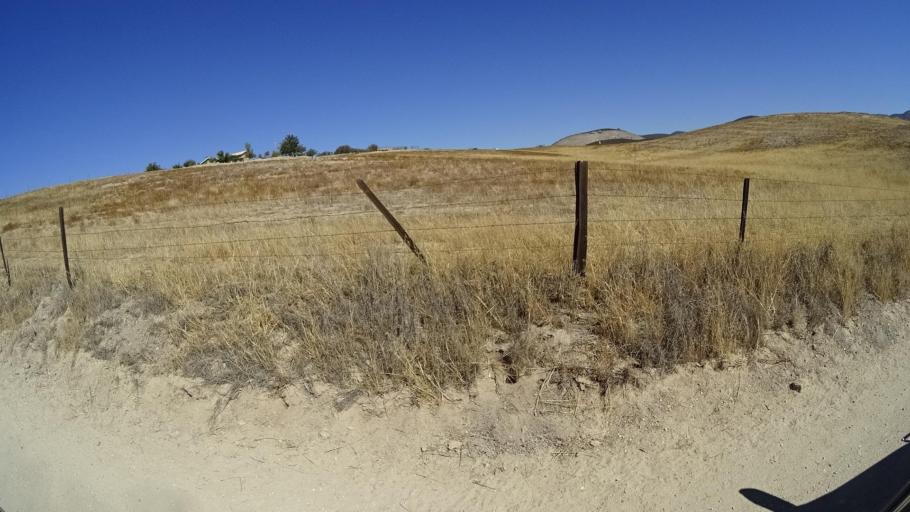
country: US
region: California
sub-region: Monterey County
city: King City
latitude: 35.9510
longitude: -121.0674
